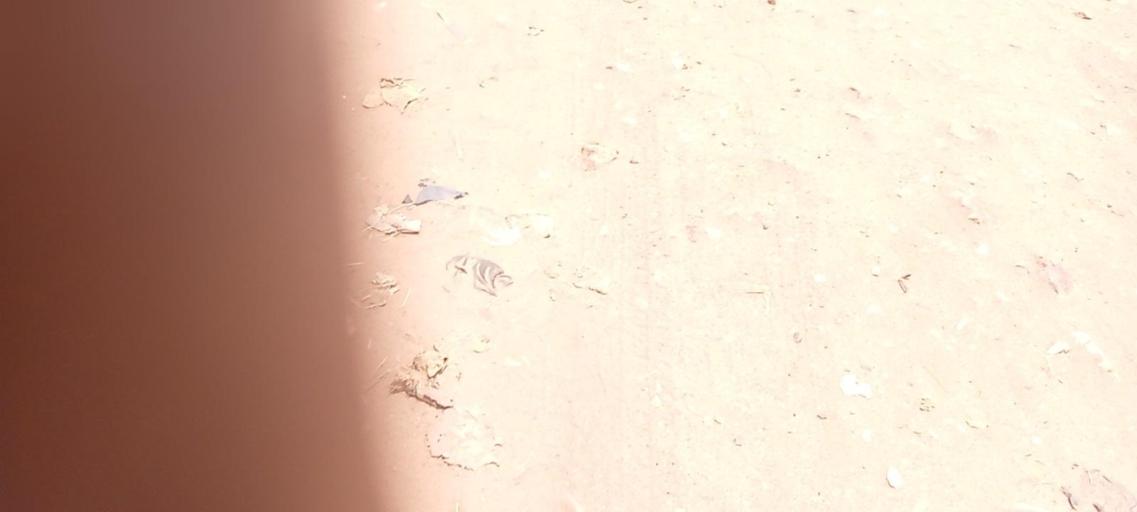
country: ZM
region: Lusaka
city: Lusaka
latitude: -15.4000
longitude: 28.3490
